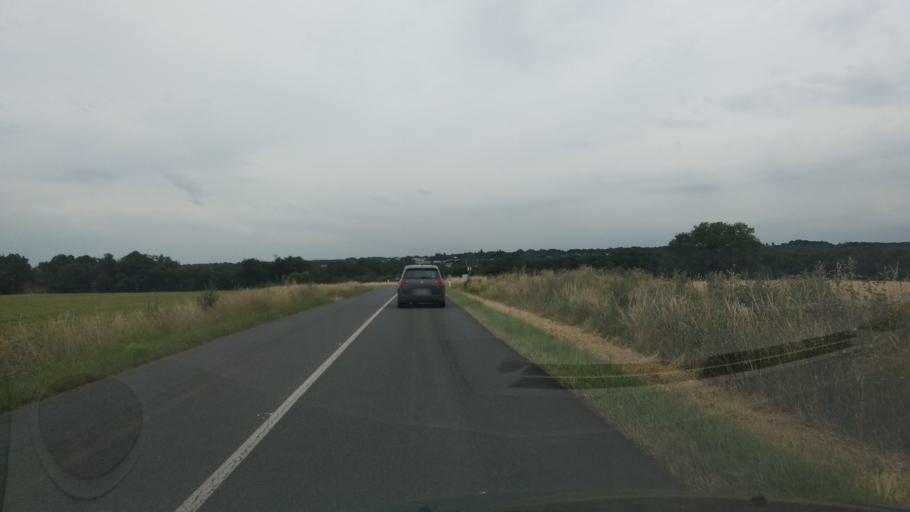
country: FR
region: Poitou-Charentes
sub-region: Departement de la Vienne
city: Biard
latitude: 46.5778
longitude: 0.2947
